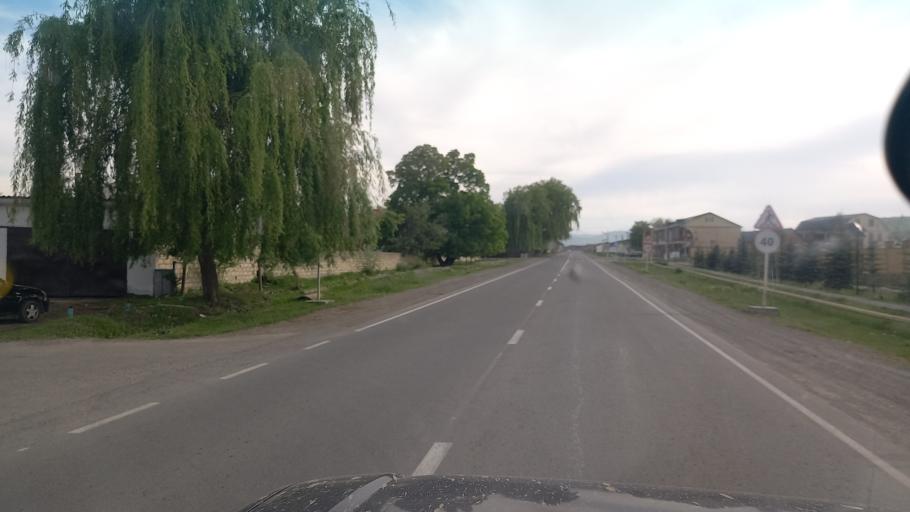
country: RU
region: Ingushetiya
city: Nesterovskaya
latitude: 43.2415
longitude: 45.0436
